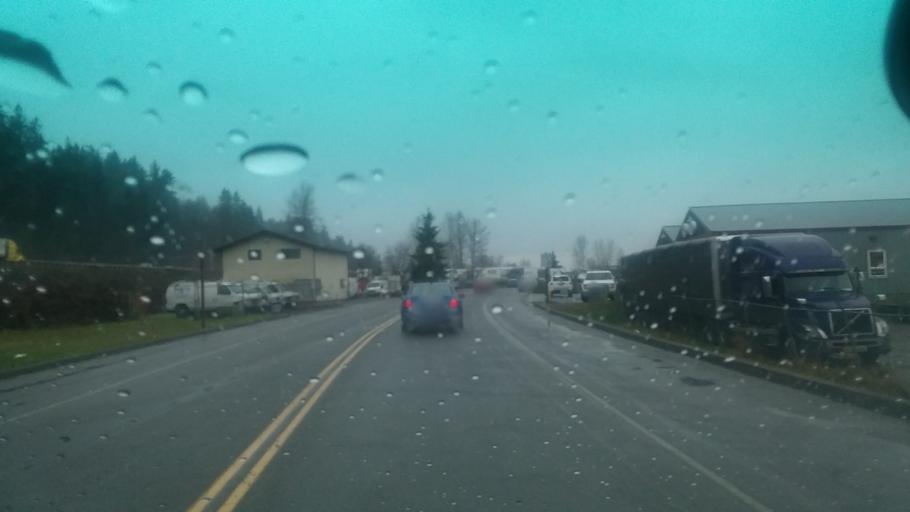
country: US
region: Washington
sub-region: King County
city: Pacific
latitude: 47.2654
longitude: -122.2609
